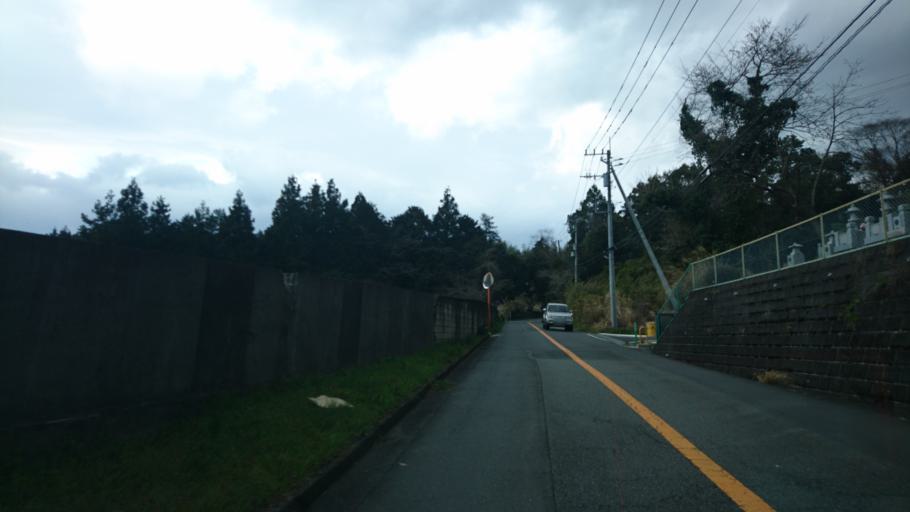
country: JP
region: Shizuoka
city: Fujinomiya
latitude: 35.2702
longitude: 138.5909
